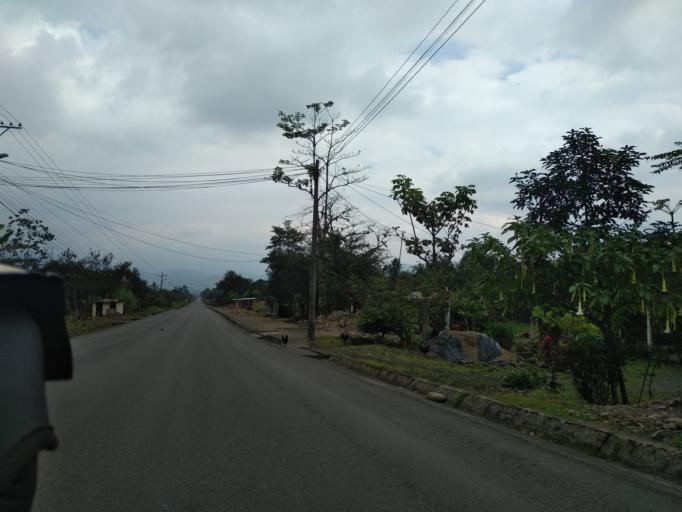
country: EC
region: Cotopaxi
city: La Mana
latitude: -0.8768
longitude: -79.1604
